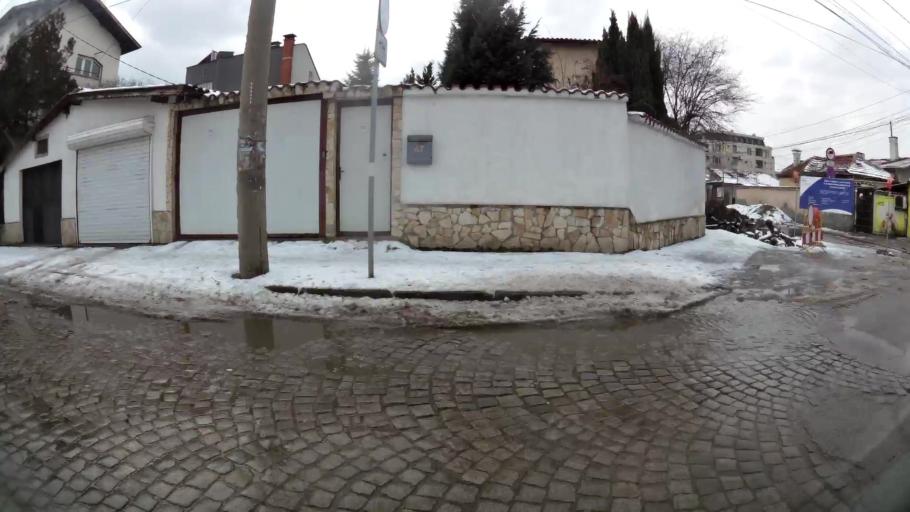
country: BG
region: Sofia-Capital
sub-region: Stolichna Obshtina
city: Sofia
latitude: 42.7067
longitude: 23.3734
